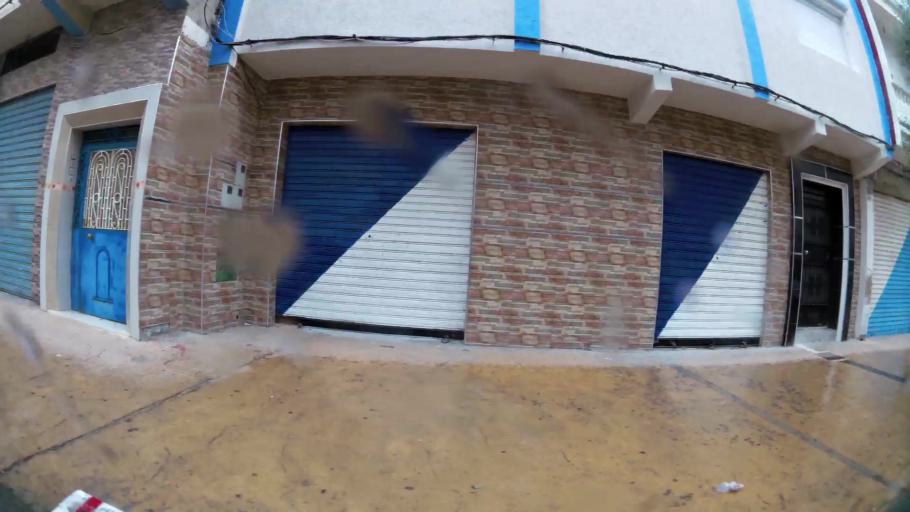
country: MA
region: Tanger-Tetouan
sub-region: Tetouan
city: Martil
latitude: 35.6230
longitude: -5.2785
